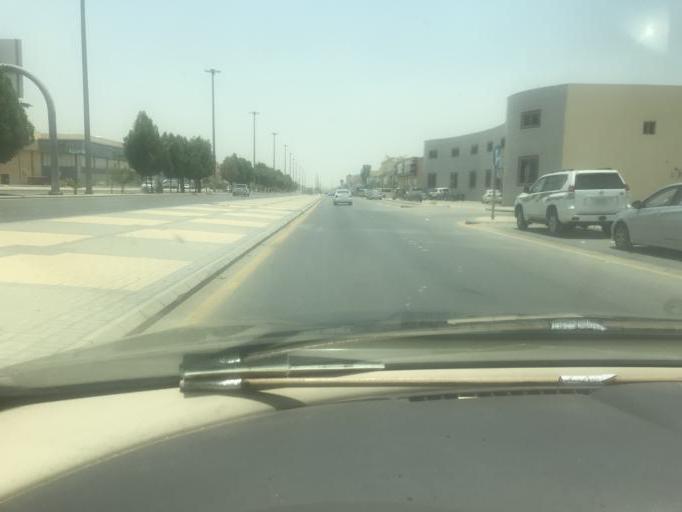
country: SA
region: Ar Riyad
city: Riyadh
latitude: 24.8199
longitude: 46.7516
